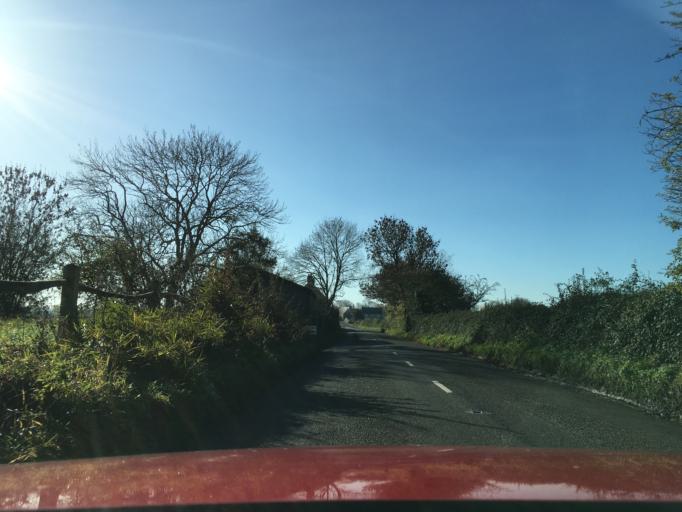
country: GB
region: England
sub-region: Somerset
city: Martock
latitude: 51.0128
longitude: -2.7600
